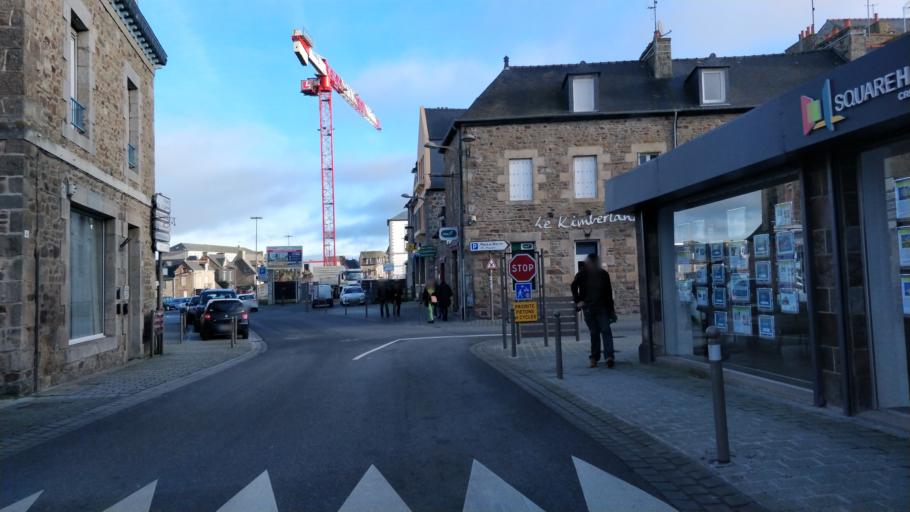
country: FR
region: Brittany
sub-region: Departement des Cotes-d'Armor
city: Lamballe
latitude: 48.4695
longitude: -2.5170
